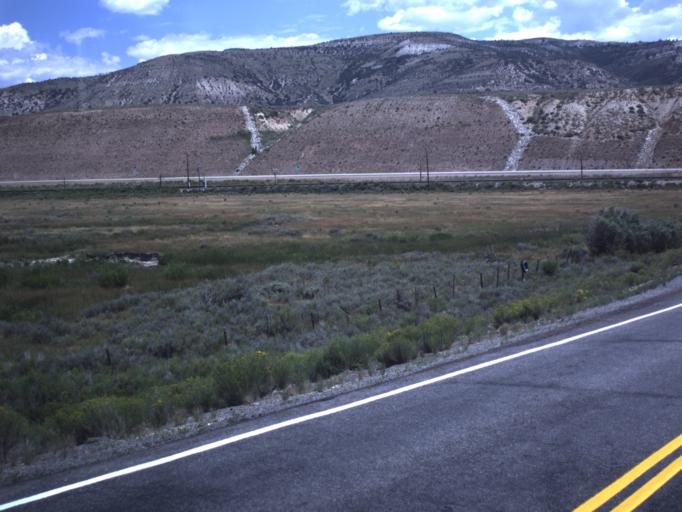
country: US
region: Utah
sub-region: Carbon County
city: Helper
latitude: 39.8609
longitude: -111.0295
